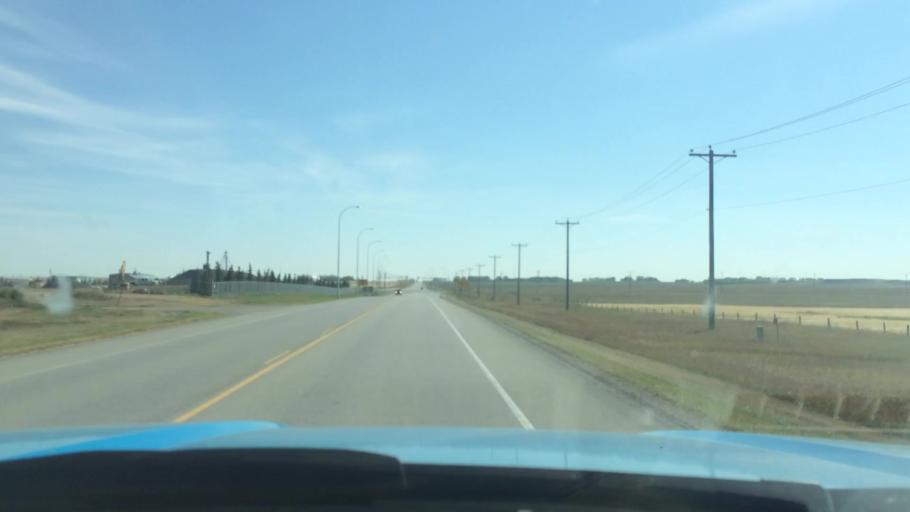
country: CA
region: Alberta
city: Airdrie
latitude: 51.2126
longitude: -113.9413
